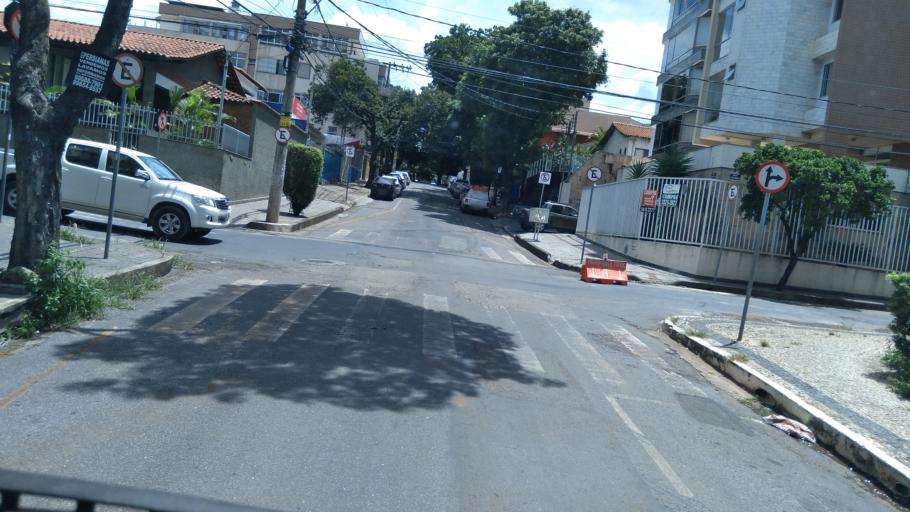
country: BR
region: Minas Gerais
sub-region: Belo Horizonte
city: Belo Horizonte
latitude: -19.9248
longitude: -43.9889
